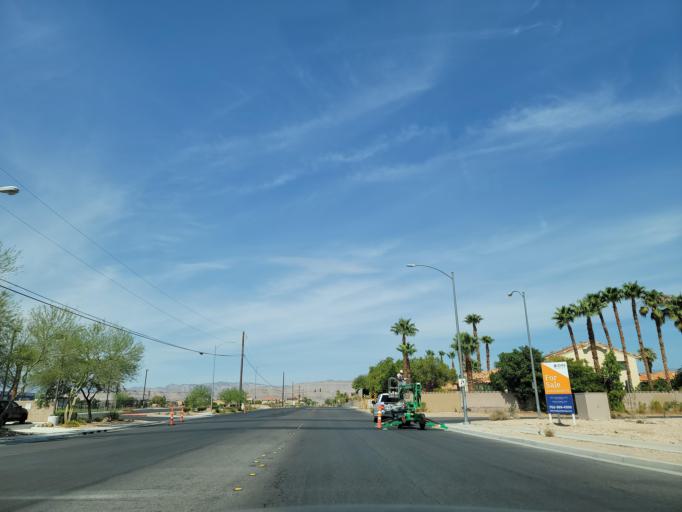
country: US
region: Nevada
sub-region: Clark County
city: Spring Valley
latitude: 36.0778
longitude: -115.2442
